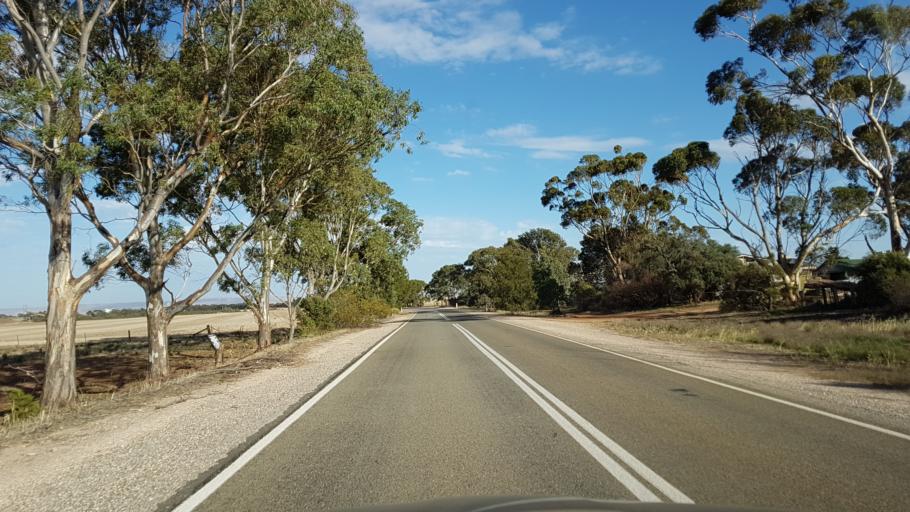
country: AU
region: South Australia
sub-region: Clare and Gilbert Valleys
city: Clare
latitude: -33.6970
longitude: 138.4395
